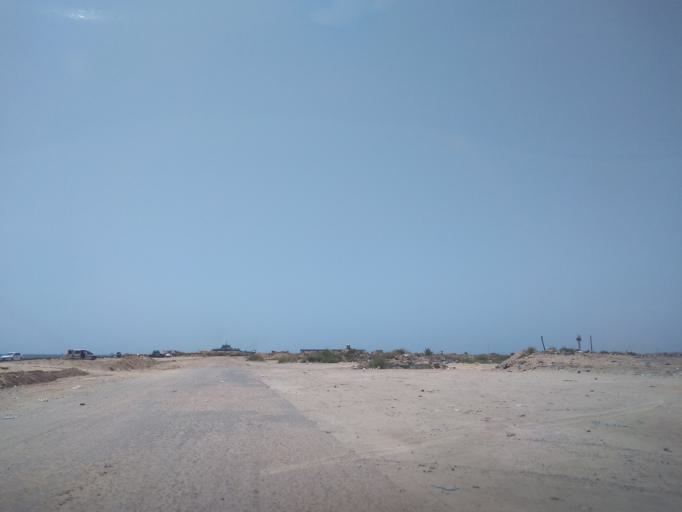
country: TN
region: Safaqis
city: Al Qarmadah
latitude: 34.7260
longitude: 10.7815
